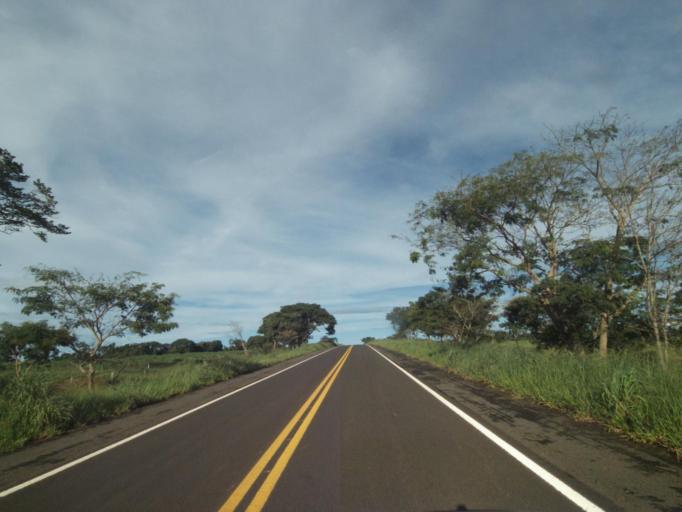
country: BR
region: Goias
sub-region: Itaberai
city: Itaberai
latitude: -15.9131
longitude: -49.5870
